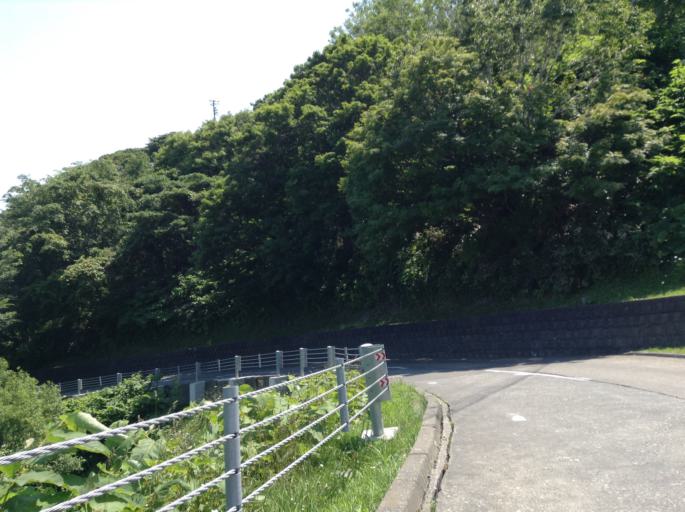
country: JP
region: Hokkaido
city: Wakkanai
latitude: 45.4214
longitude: 141.6693
